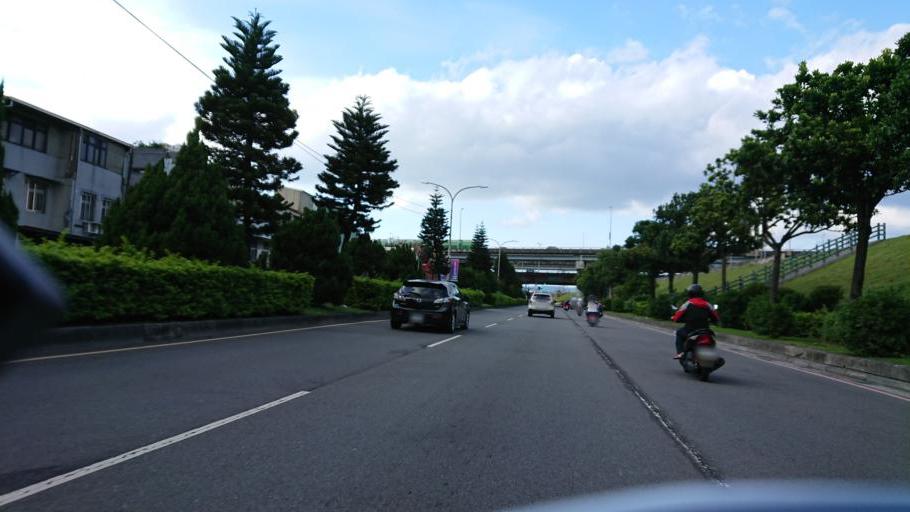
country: TW
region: Taipei
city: Taipei
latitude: 25.0758
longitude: 121.5025
